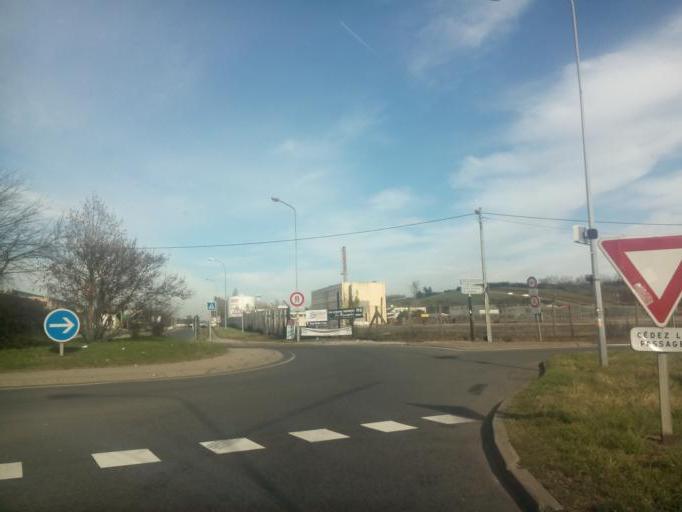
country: FR
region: Rhone-Alpes
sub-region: Departement du Rhone
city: Chaponost
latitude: 45.6983
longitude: 4.7665
